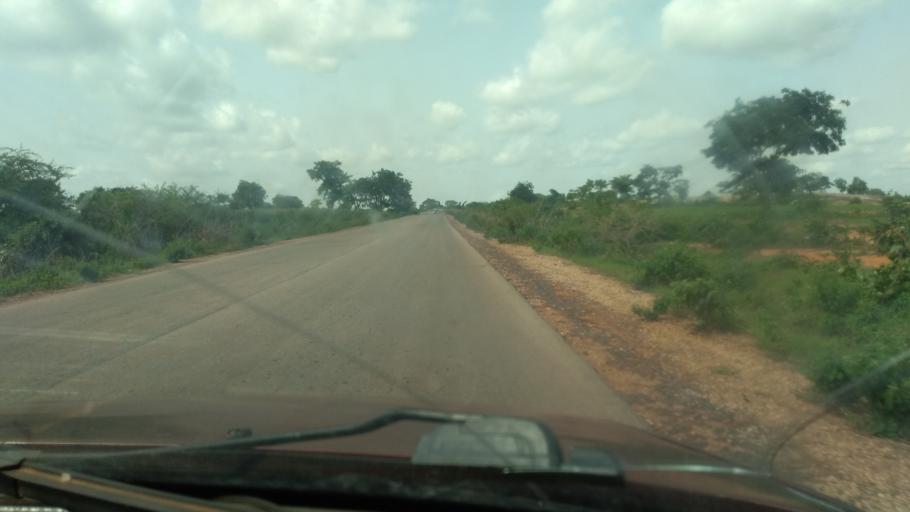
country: NG
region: Katsina
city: Sabuwa
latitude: 11.0517
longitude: 7.1613
